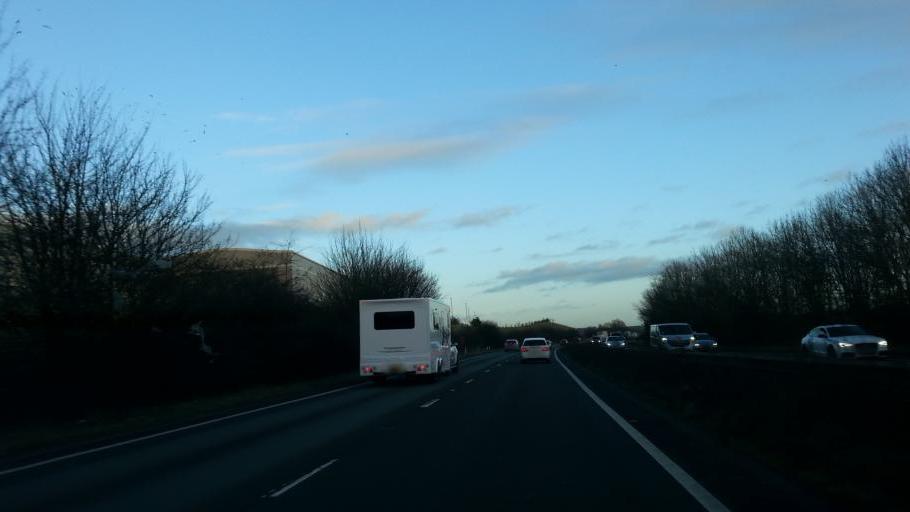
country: GB
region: England
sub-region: Northamptonshire
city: Thrapston
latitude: 52.3920
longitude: -0.5728
